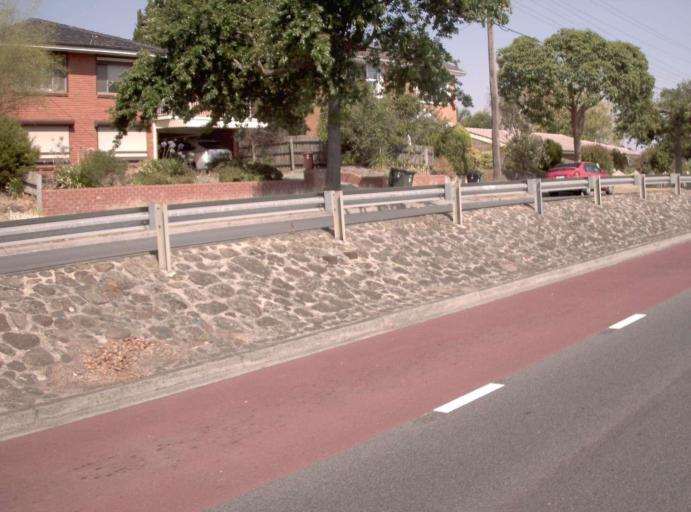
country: AU
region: Victoria
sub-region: Manningham
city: Templestowe Lower
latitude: -37.7770
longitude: 145.1192
